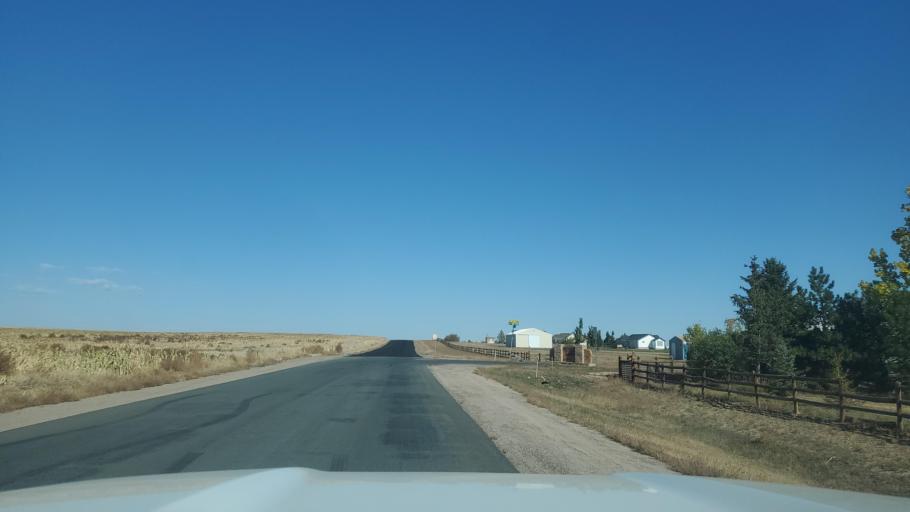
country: US
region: Colorado
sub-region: Adams County
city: Bennett
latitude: 39.7396
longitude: -104.3773
